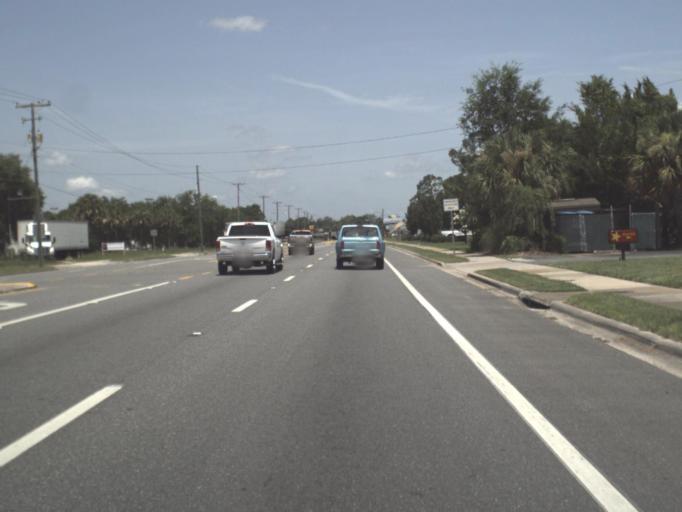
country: US
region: Florida
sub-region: Taylor County
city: Perry
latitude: 30.0991
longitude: -83.5840
